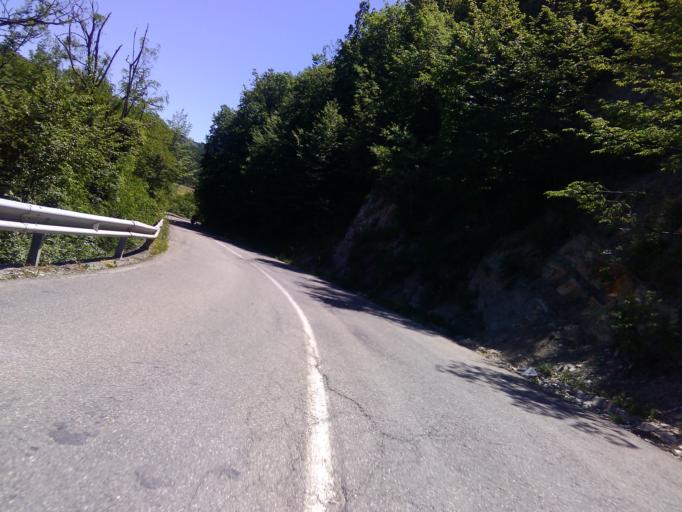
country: IT
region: Emilia-Romagna
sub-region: Provincia di Parma
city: Terenzo
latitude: 44.5822
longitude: 10.0804
